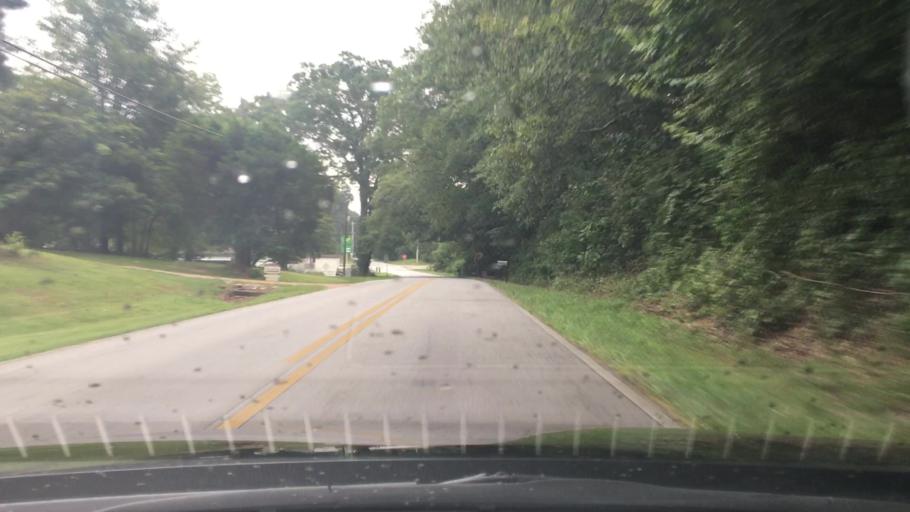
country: US
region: Georgia
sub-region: Spalding County
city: Experiment
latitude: 33.2801
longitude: -84.3844
